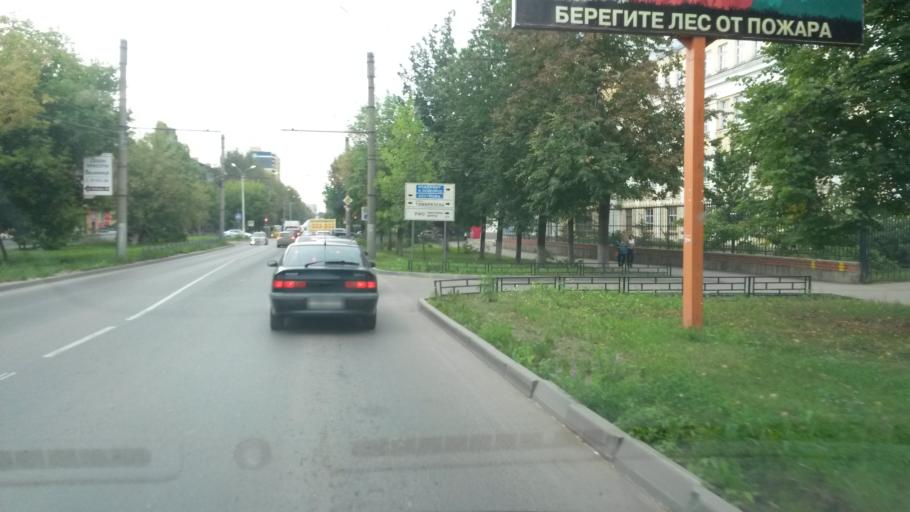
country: RU
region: Ivanovo
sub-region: Gorod Ivanovo
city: Ivanovo
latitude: 57.0195
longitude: 40.9574
